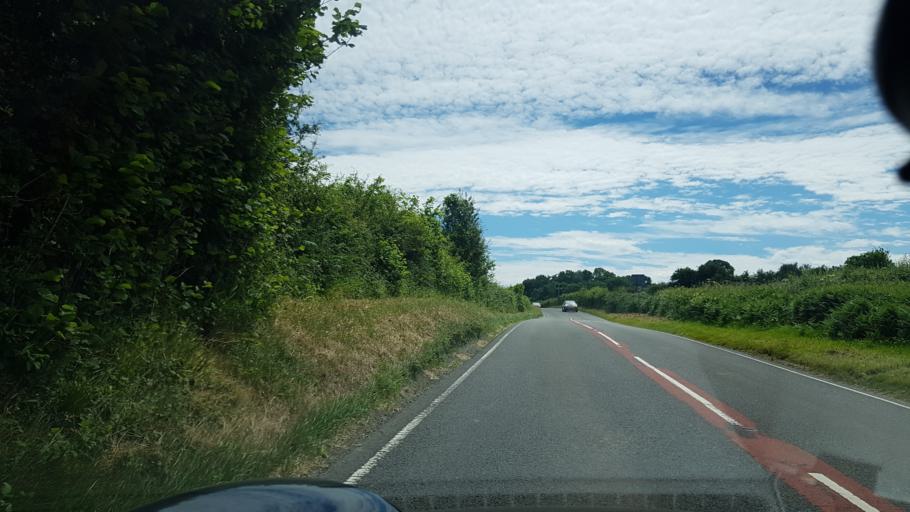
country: GB
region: Wales
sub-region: Carmarthenshire
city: Saint Clears
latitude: 51.8030
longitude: -4.4945
